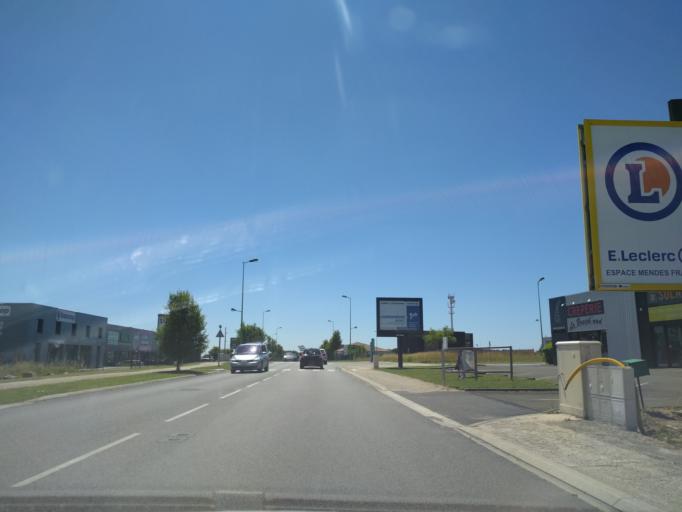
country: FR
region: Poitou-Charentes
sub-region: Departement des Deux-Sevres
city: Chauray
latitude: 46.3376
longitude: -0.3984
